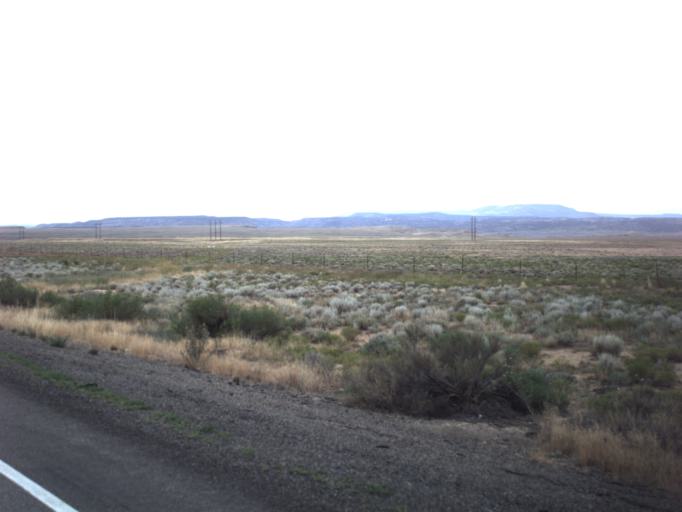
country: US
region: Utah
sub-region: Carbon County
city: East Carbon City
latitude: 39.4948
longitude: -110.5224
